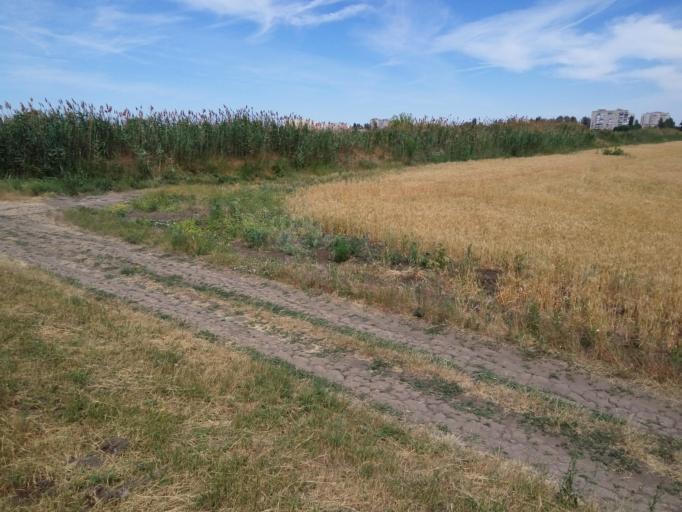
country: RU
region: Rostov
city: Bataysk
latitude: 47.1212
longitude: 39.7227
